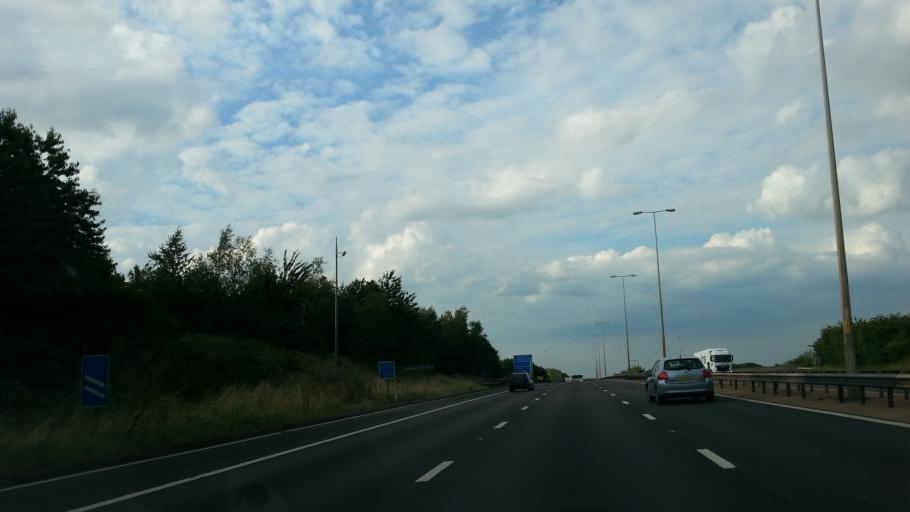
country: GB
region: England
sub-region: Worcestershire
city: Kempsey
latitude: 52.1616
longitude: -2.1868
